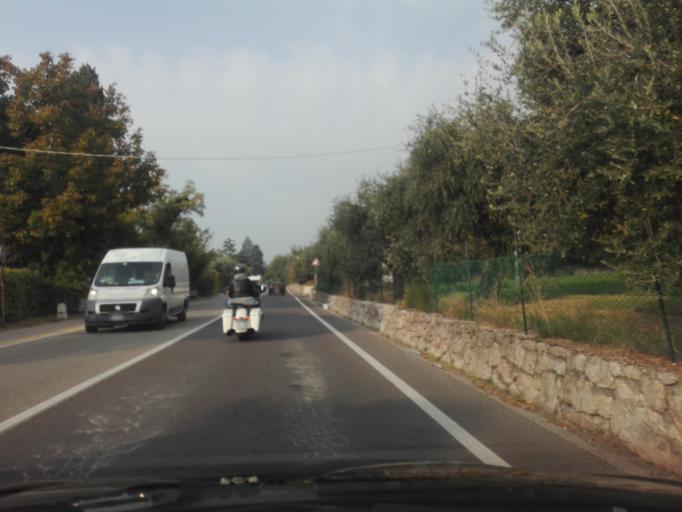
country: IT
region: Veneto
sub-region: Provincia di Verona
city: Lazise
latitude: 45.5208
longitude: 10.7298
